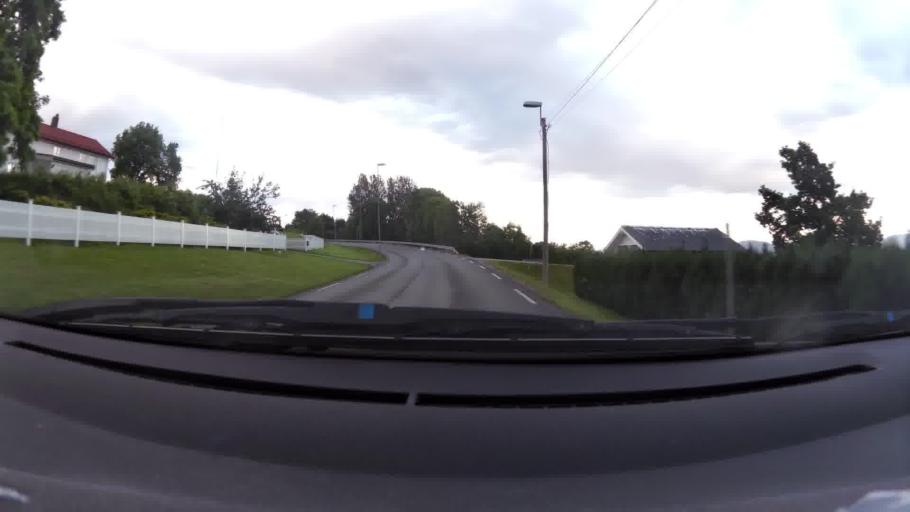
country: NO
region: More og Romsdal
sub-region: Molde
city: Molde
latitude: 62.7507
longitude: 7.2503
